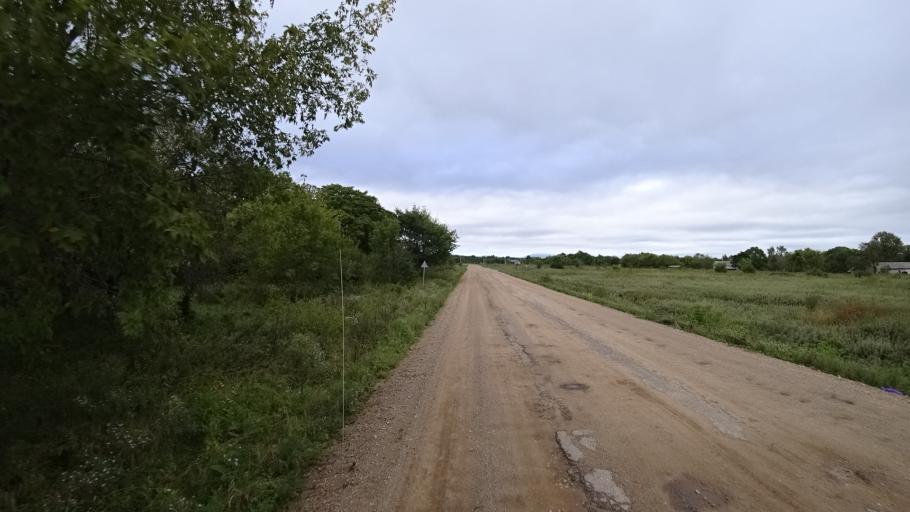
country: RU
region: Primorskiy
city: Rettikhovka
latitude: 44.1324
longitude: 132.6457
